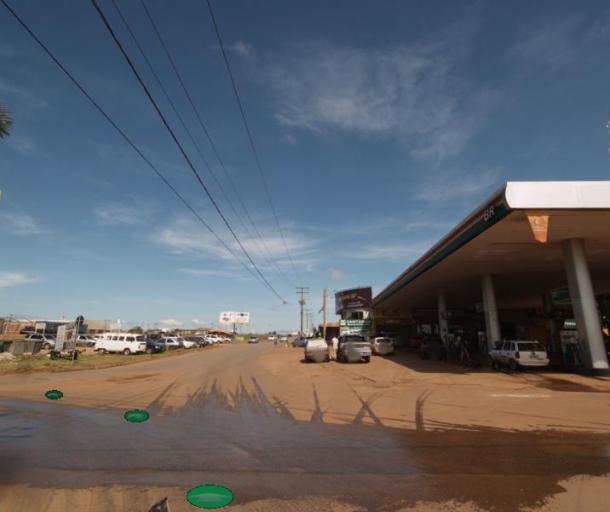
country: BR
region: Federal District
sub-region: Brasilia
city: Brasilia
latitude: -15.7354
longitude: -48.2832
